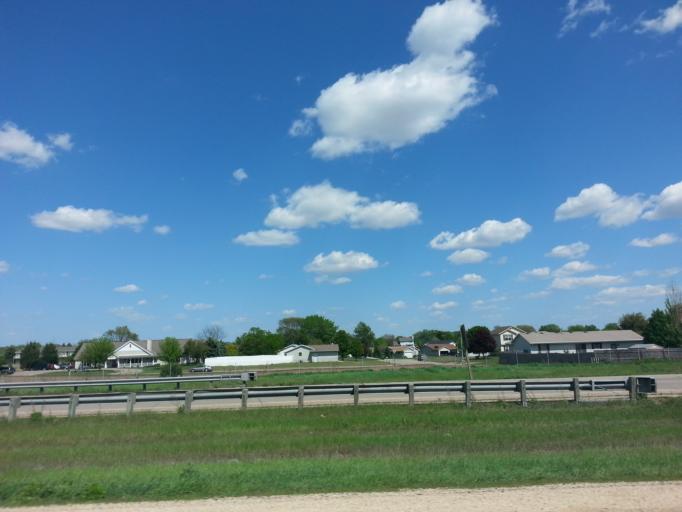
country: US
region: Wisconsin
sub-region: Rock County
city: Janesville
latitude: 42.7121
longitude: -88.9843
